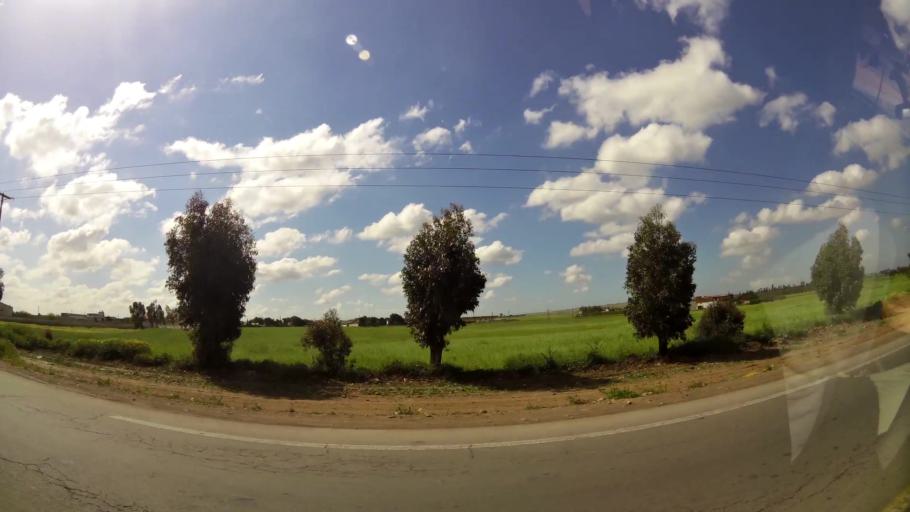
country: MA
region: Grand Casablanca
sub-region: Mediouna
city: Mediouna
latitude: 33.4150
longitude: -7.5314
